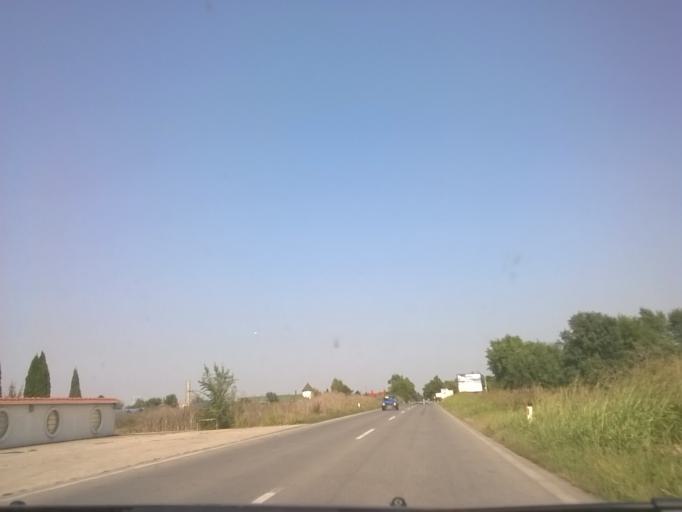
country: RS
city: Pavlis
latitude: 45.1003
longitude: 21.2721
